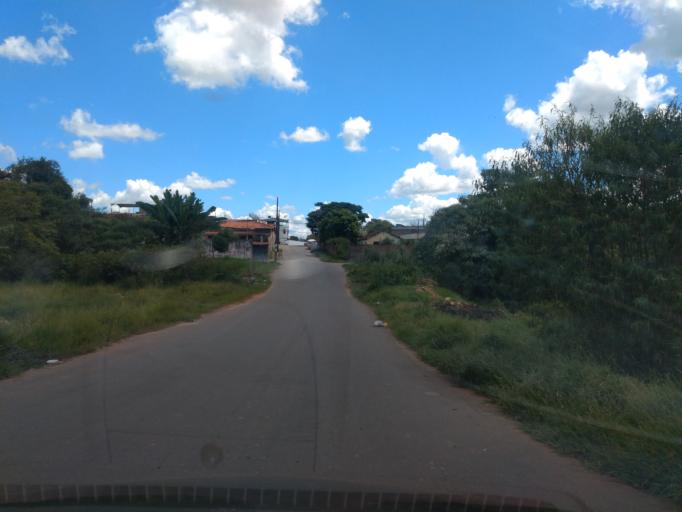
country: BR
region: Minas Gerais
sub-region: Tres Coracoes
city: Tres Coracoes
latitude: -21.6800
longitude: -45.2427
